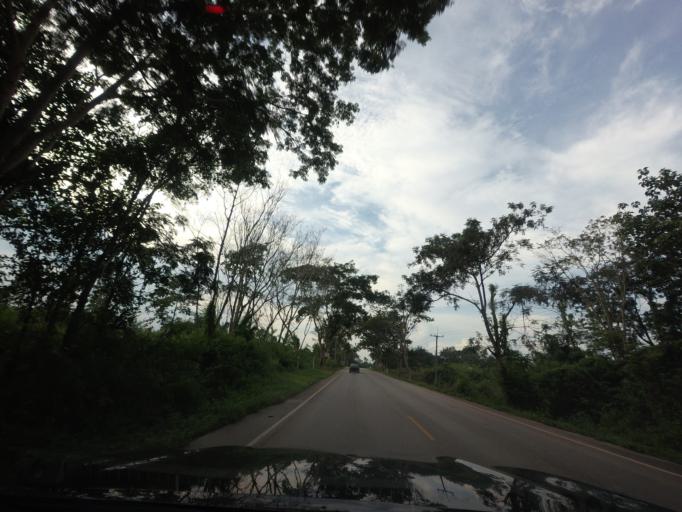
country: TH
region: Changwat Udon Thani
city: Nam Som
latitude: 17.8364
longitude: 102.2597
